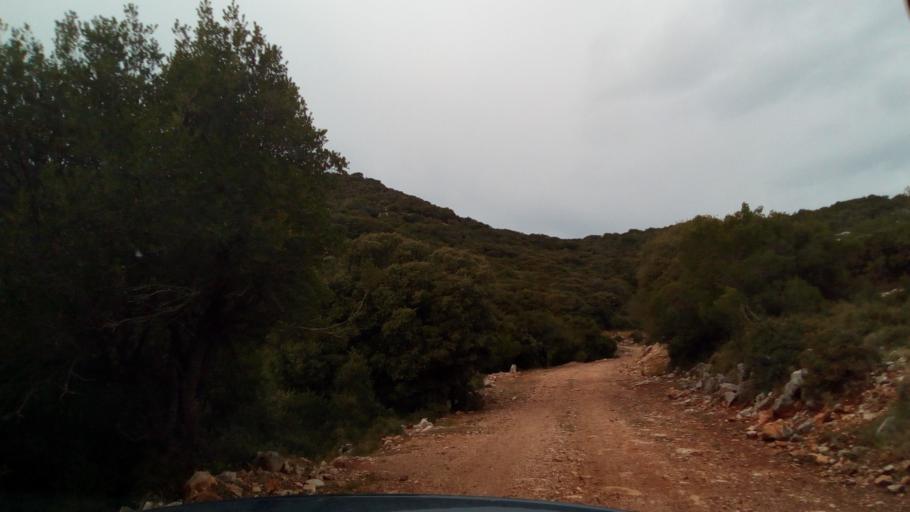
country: GR
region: West Greece
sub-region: Nomos Achaias
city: Kamarai
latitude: 38.4109
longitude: 22.0470
